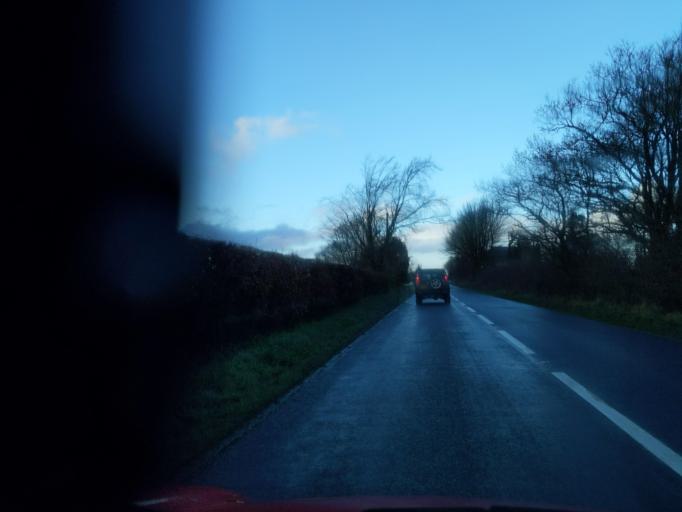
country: GB
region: England
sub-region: Devon
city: Okehampton
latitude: 50.7581
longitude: -4.0236
